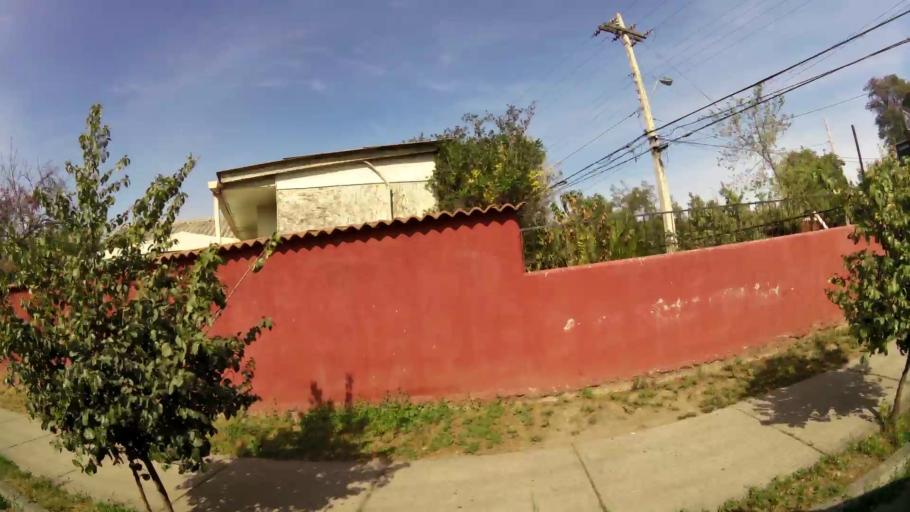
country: CL
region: Santiago Metropolitan
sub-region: Provincia de Santiago
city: Villa Presidente Frei, Nunoa, Santiago, Chile
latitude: -33.5181
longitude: -70.5909
